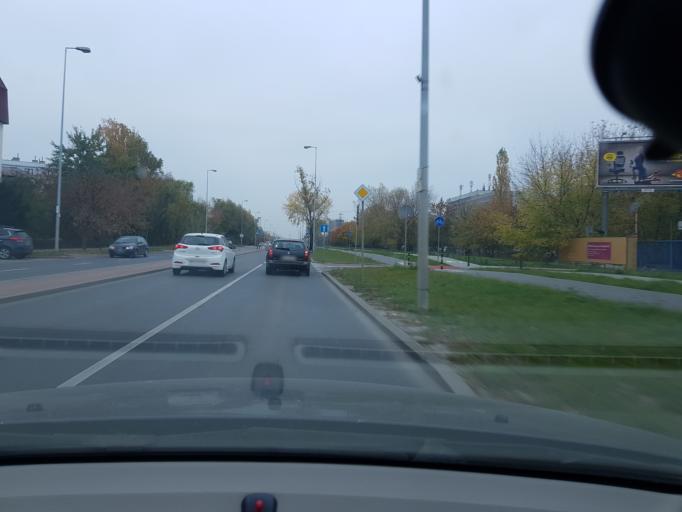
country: PL
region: Masovian Voivodeship
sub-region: Warszawa
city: Ursynow
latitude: 52.1459
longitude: 21.0276
